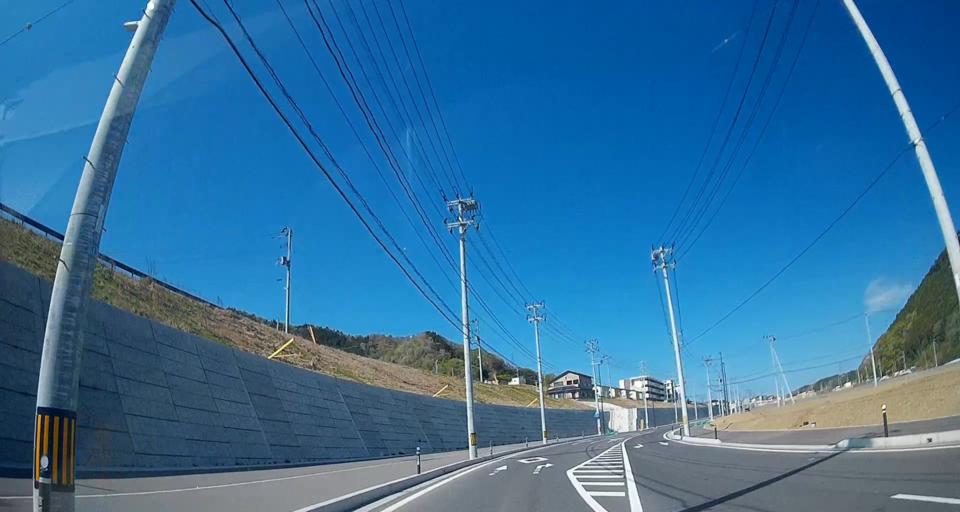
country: JP
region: Miyagi
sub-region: Oshika Gun
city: Onagawa Cho
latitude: 38.4409
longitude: 141.4461
